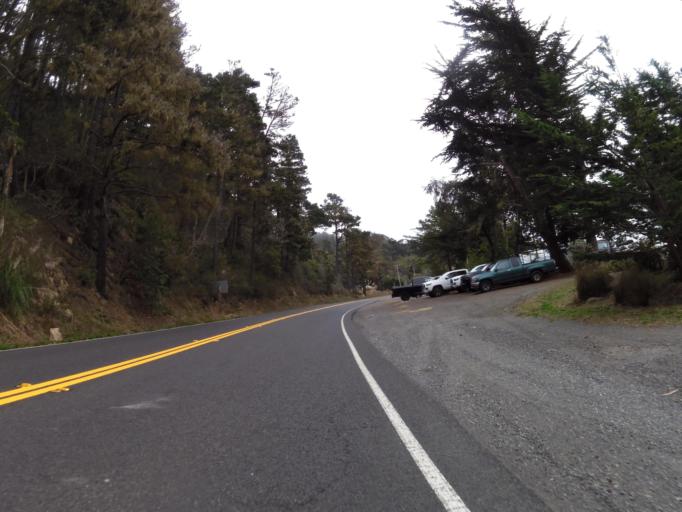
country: US
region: California
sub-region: Sonoma County
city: Sea Ranch
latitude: 38.5333
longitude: -123.2732
